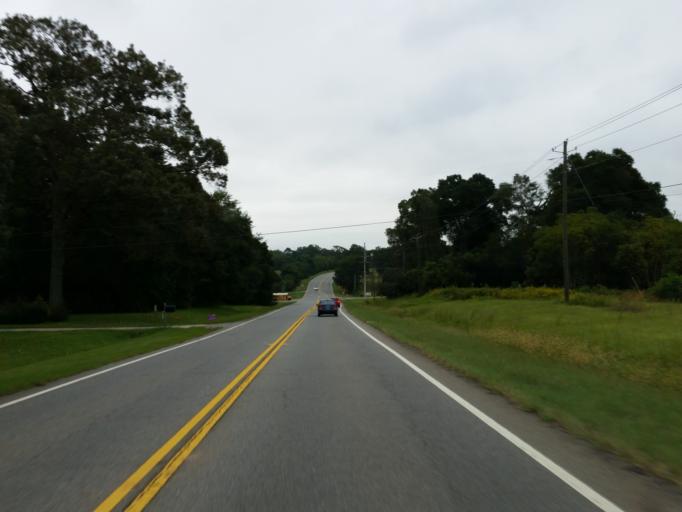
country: US
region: Georgia
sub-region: Houston County
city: Perry
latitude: 32.4814
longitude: -83.7621
